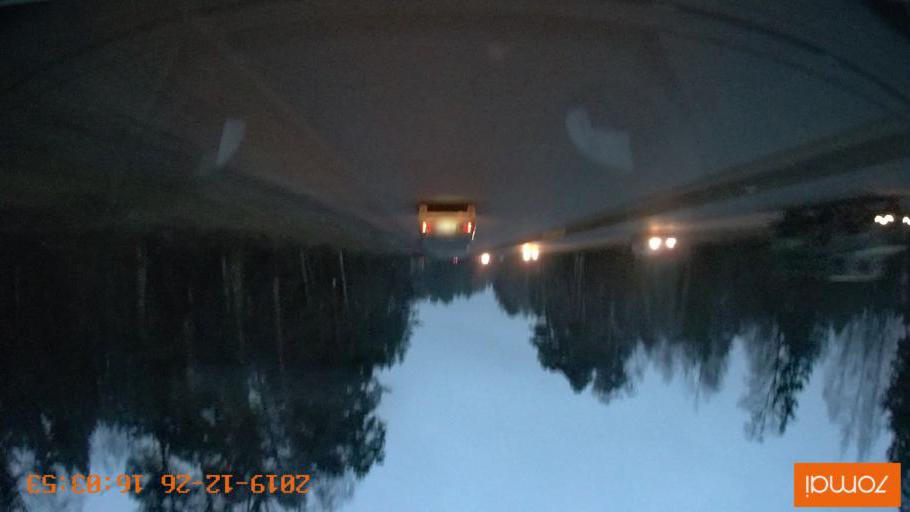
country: RU
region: Jaroslavl
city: Rybinsk
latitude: 58.0099
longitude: 38.8596
